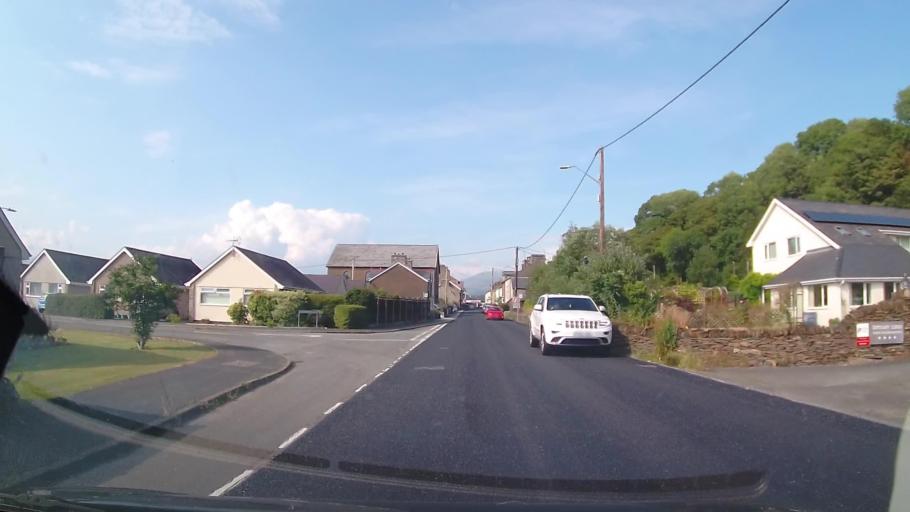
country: GB
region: Wales
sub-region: Gwynedd
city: Penrhyndeudraeth
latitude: 52.9020
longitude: -4.0658
